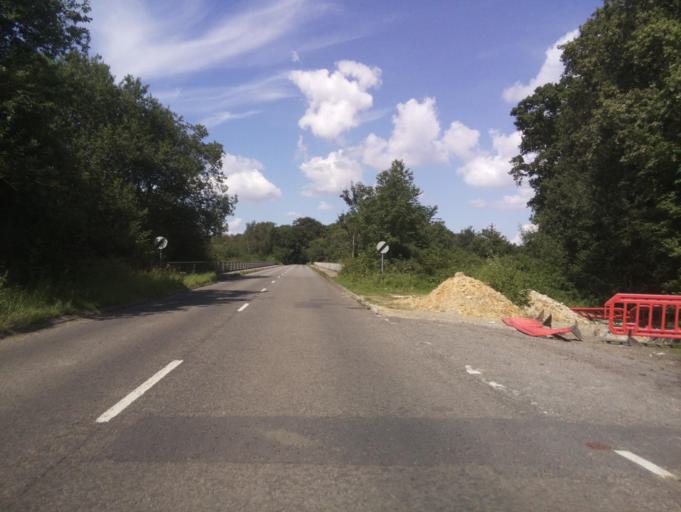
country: GB
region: England
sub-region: West Berkshire
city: Winterbourne
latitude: 51.4280
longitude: -1.3342
